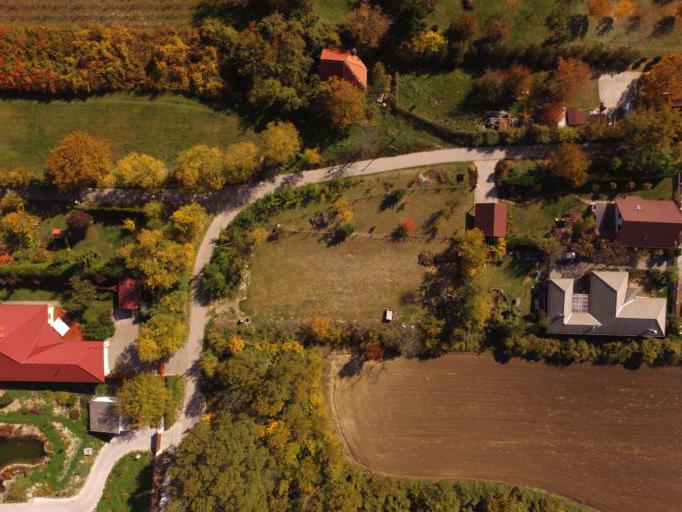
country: HU
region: Fejer
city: Many
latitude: 47.5195
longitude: 18.6194
